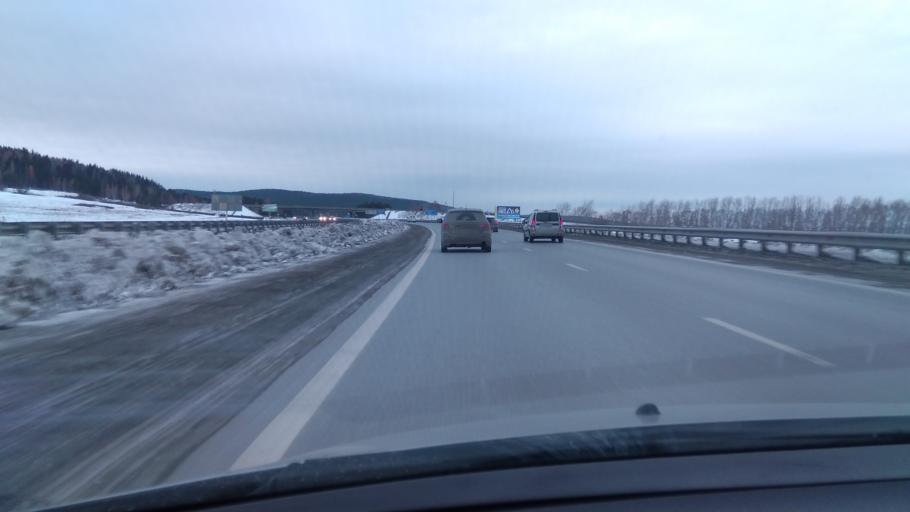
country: RU
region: Sverdlovsk
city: Aramil
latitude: 56.6912
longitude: 60.7629
